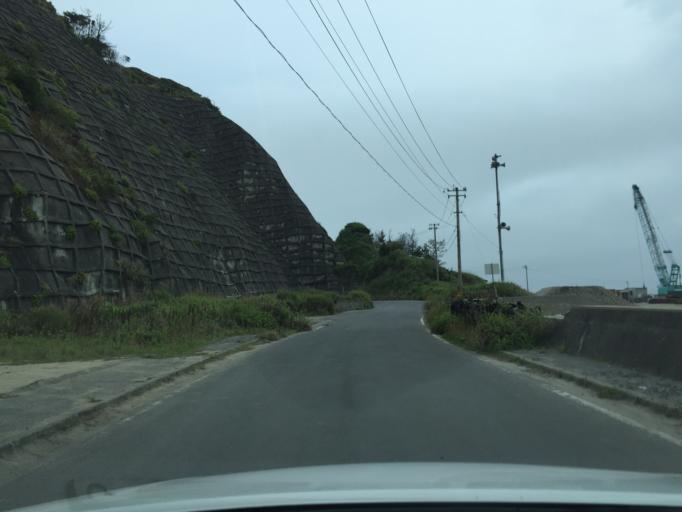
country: JP
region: Fukushima
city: Iwaki
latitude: 36.9928
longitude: 140.9756
